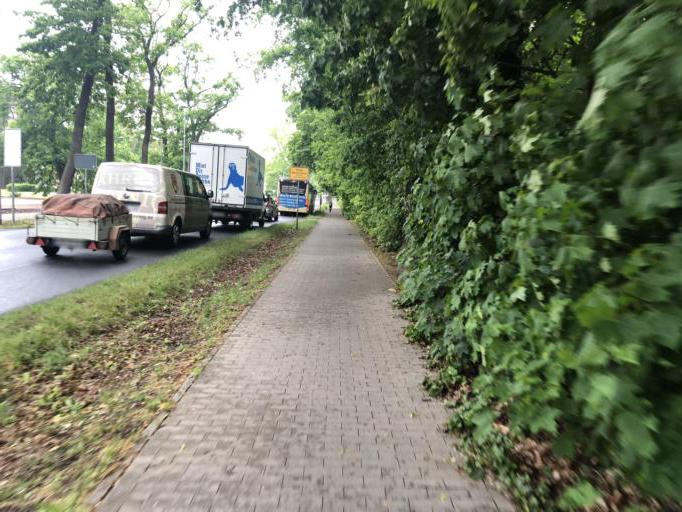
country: DE
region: Brandenburg
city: Konigs Wusterhausen
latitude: 52.2880
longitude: 13.6294
